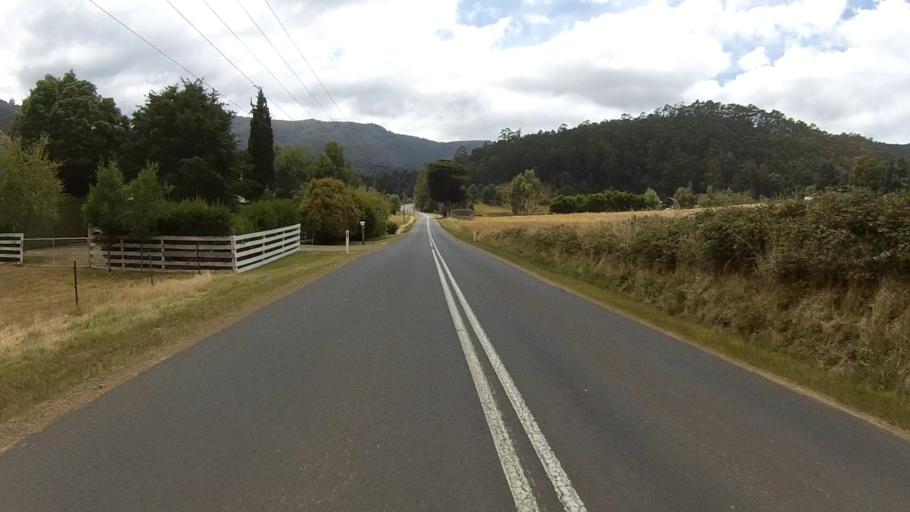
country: AU
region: Tasmania
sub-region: Huon Valley
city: Cygnet
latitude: -43.1355
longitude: 147.1543
